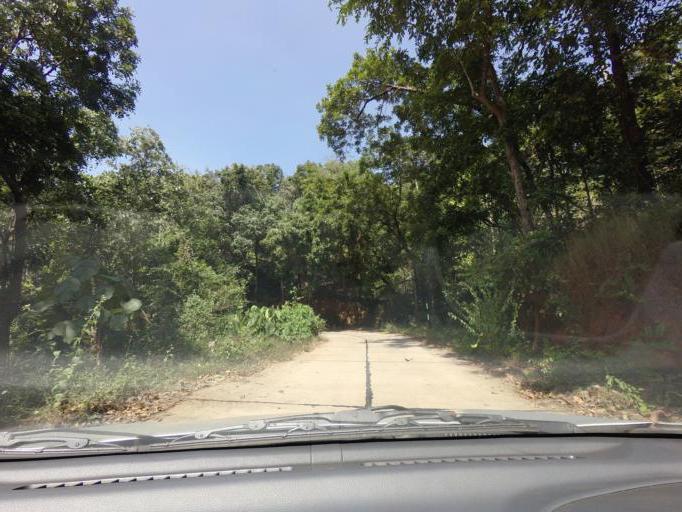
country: IN
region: Karnataka
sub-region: Kodagu
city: Somvarpet
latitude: 12.6958
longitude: 75.6348
